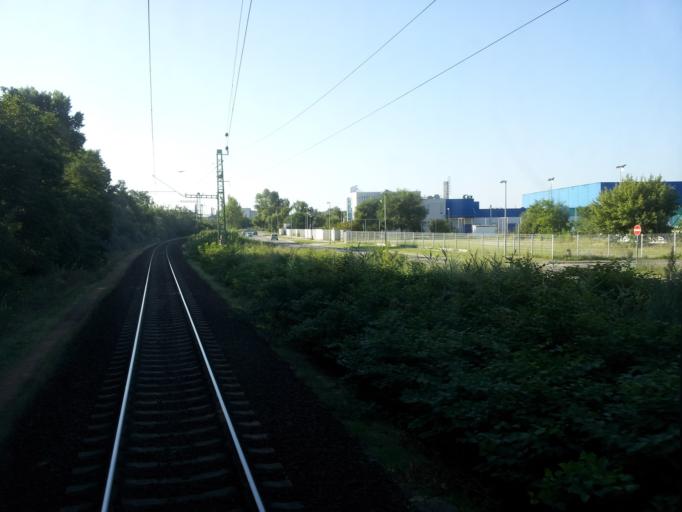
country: HU
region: Budapest
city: Budapest XX. keruelet
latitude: 47.4307
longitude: 19.1004
